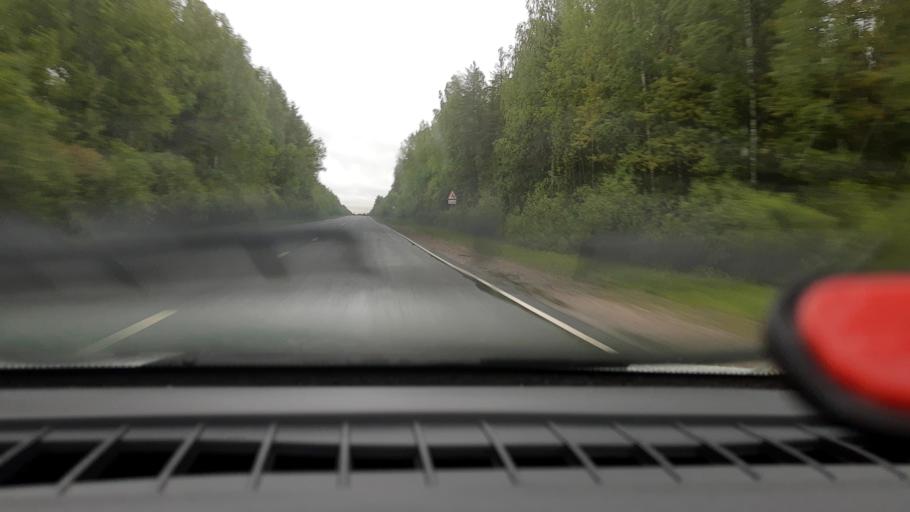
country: RU
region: Nizjnij Novgorod
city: Vladimirskoye
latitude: 56.9431
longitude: 45.0812
